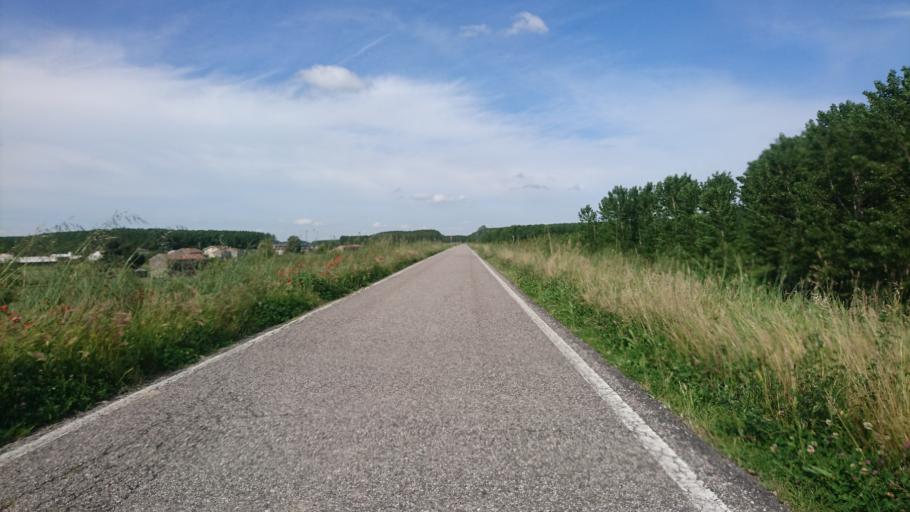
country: IT
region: Veneto
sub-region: Provincia di Rovigo
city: Melara
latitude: 45.0519
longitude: 11.1968
